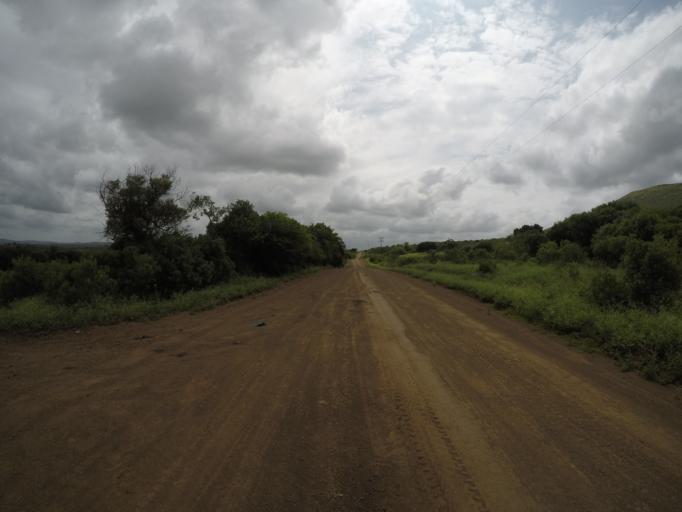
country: ZA
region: KwaZulu-Natal
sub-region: uThungulu District Municipality
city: Empangeni
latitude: -28.5751
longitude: 31.8713
